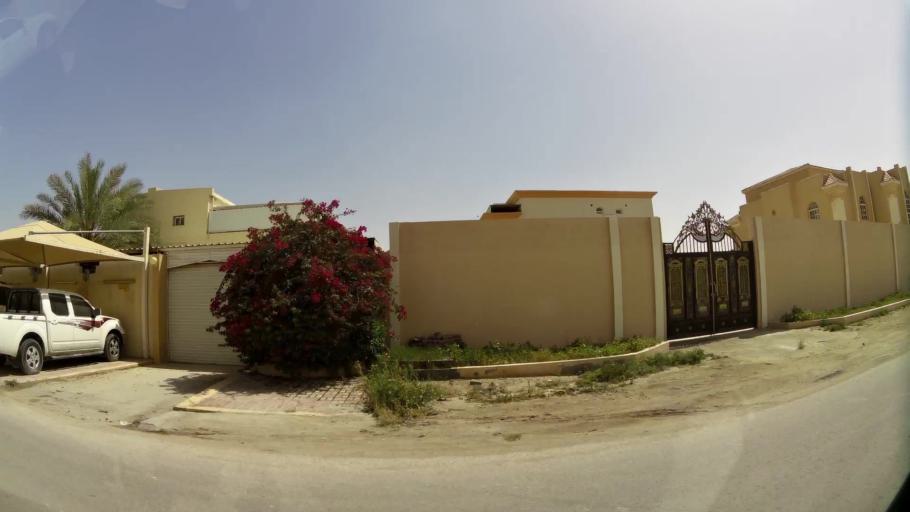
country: QA
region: Baladiyat Umm Salal
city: Umm Salal Muhammad
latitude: 25.3816
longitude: 51.4170
